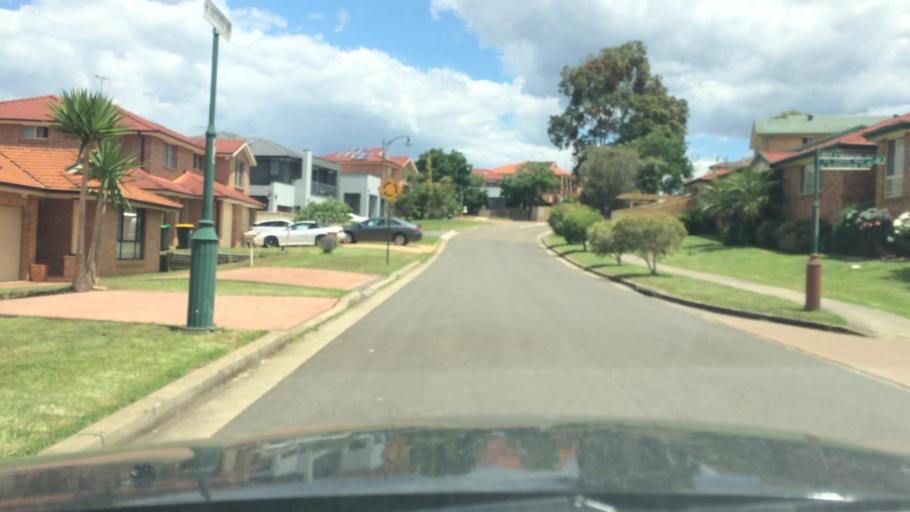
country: AU
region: New South Wales
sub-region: Campbelltown Municipality
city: Denham Court
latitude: -33.9402
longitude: 150.8345
